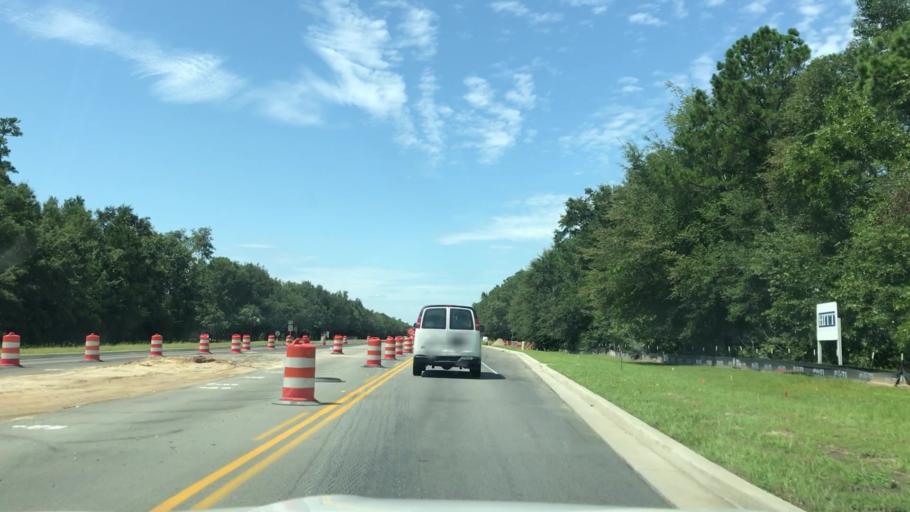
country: US
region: South Carolina
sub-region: Charleston County
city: North Charleston
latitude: 32.9068
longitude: -79.9061
